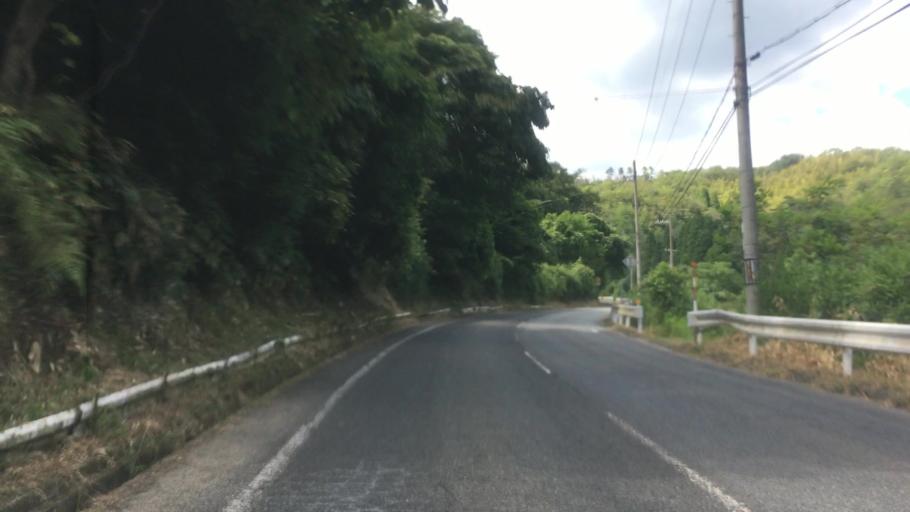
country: JP
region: Hyogo
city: Toyooka
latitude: 35.5117
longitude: 134.7806
